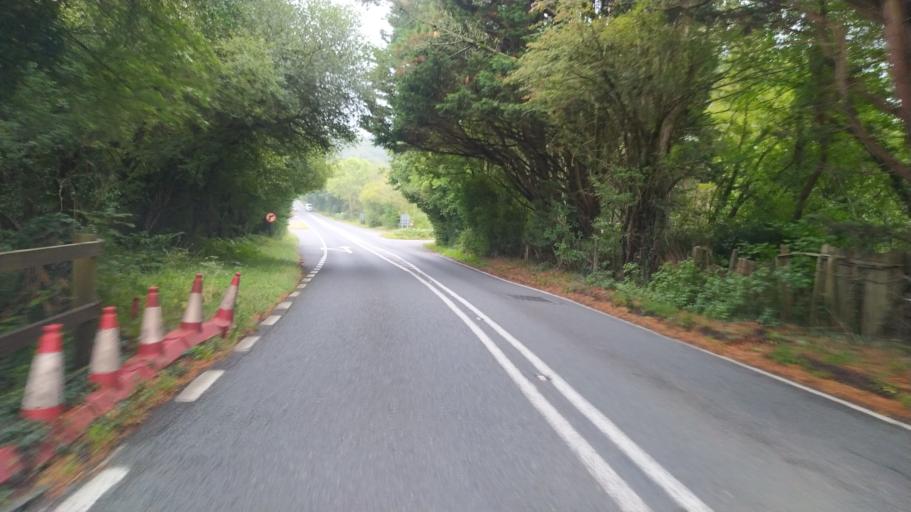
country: GB
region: England
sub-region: Hampshire
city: New Milton
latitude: 50.8049
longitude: -1.6716
